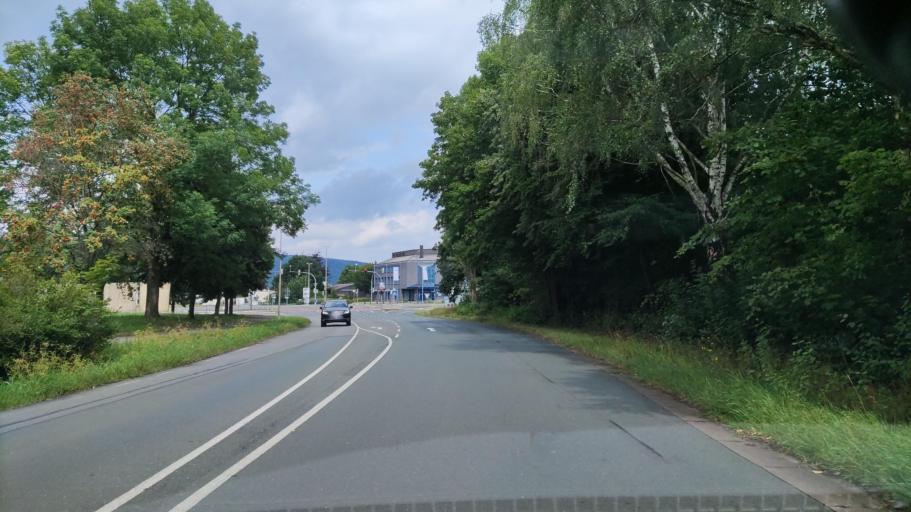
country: DE
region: Lower Saxony
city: Holzminden
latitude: 51.8378
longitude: 9.4679
